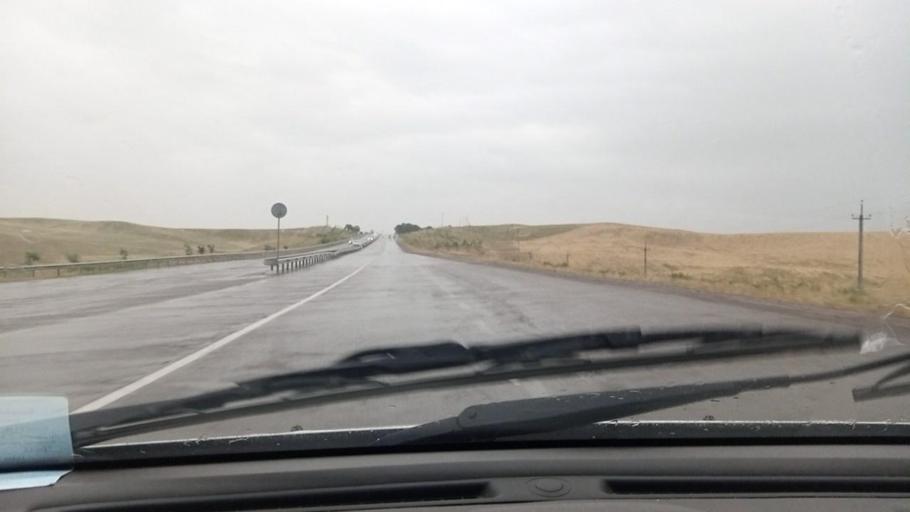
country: UZ
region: Toshkent
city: Ohangaron
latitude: 40.9684
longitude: 69.5492
